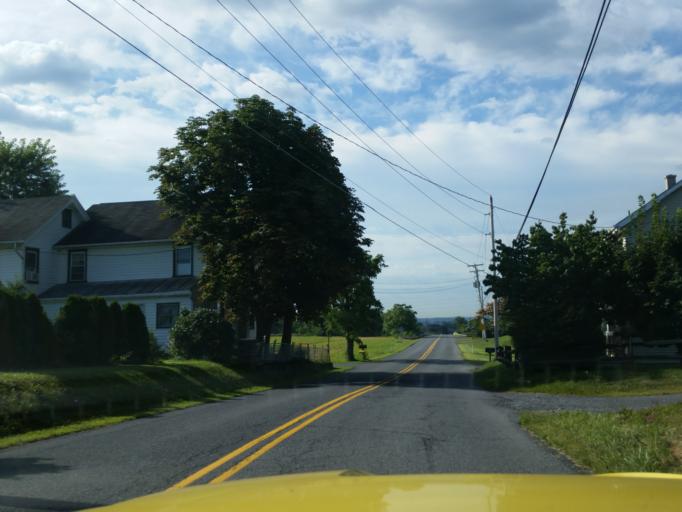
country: US
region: Pennsylvania
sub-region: Lebanon County
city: Fredericksburg
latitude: 40.4545
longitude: -76.4341
